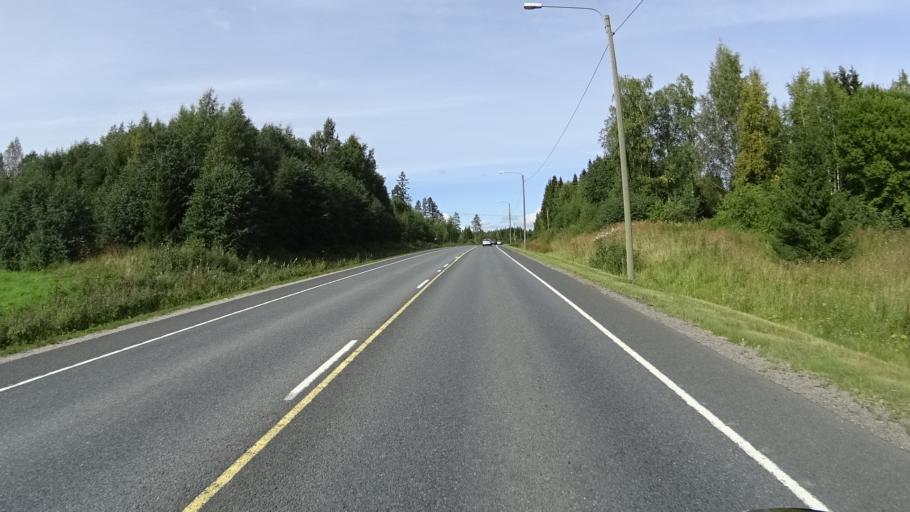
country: FI
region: Pirkanmaa
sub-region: Tampere
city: Haemeenkyroe
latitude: 61.6609
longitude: 23.1658
